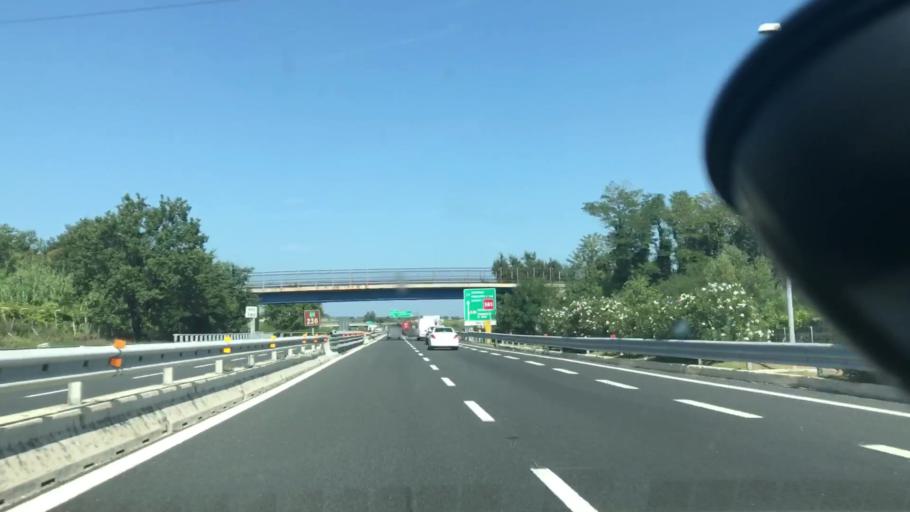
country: IT
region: Abruzzo
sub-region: Provincia di Chieti
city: Francavilla al Mare
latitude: 42.3906
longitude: 14.2887
